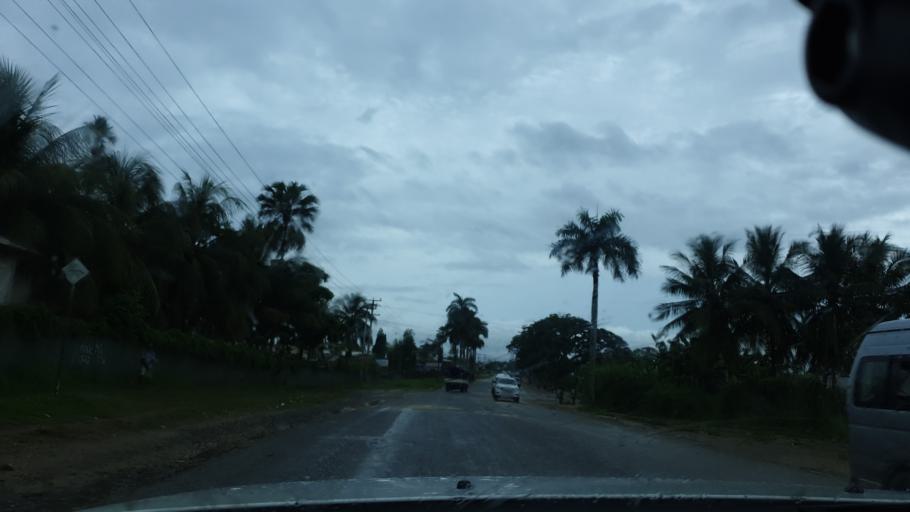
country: PG
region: Madang
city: Madang
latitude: -5.2308
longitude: 145.7955
